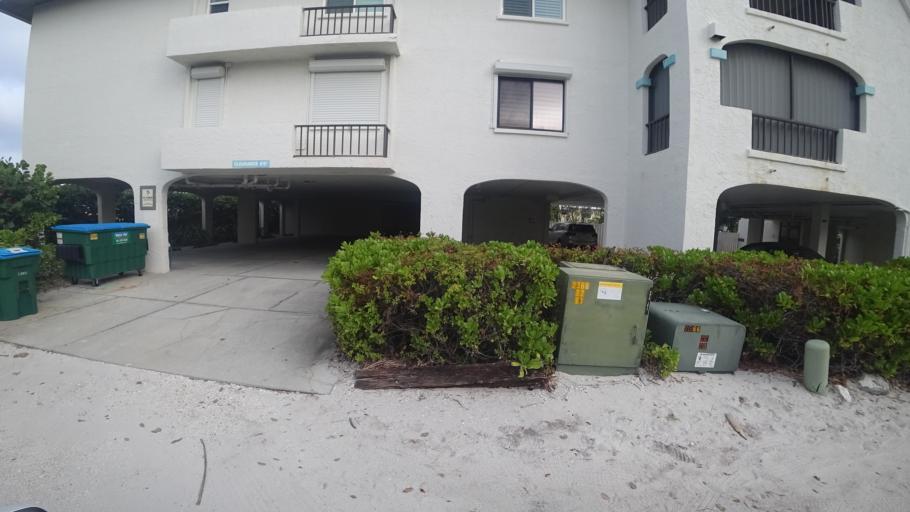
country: US
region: Florida
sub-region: Manatee County
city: Holmes Beach
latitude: 27.4848
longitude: -82.7060
